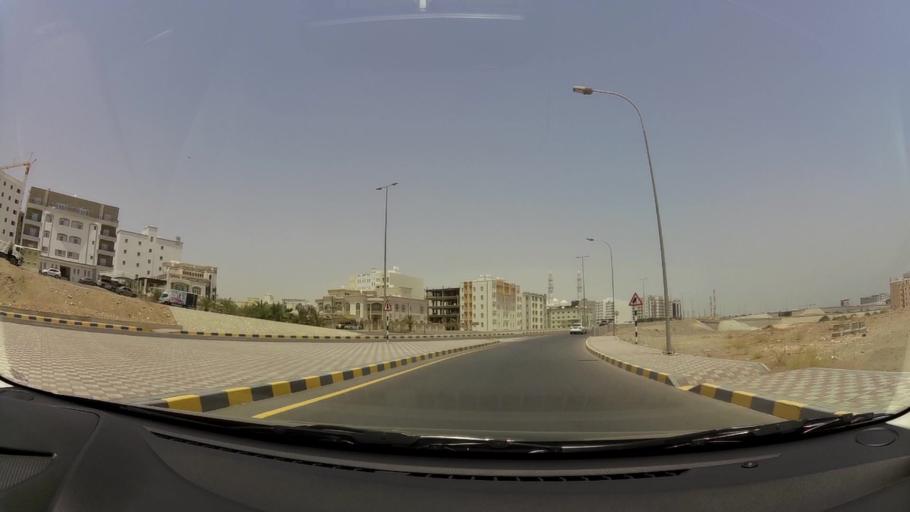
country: OM
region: Muhafazat Masqat
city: Bawshar
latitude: 23.5770
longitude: 58.4216
